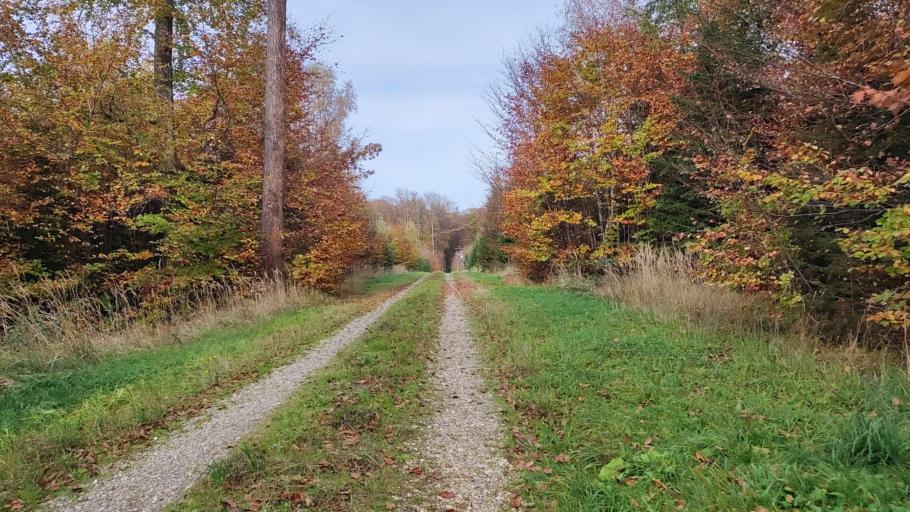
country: DE
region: Bavaria
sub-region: Swabia
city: Langenneufnach
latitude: 48.2690
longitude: 10.5700
